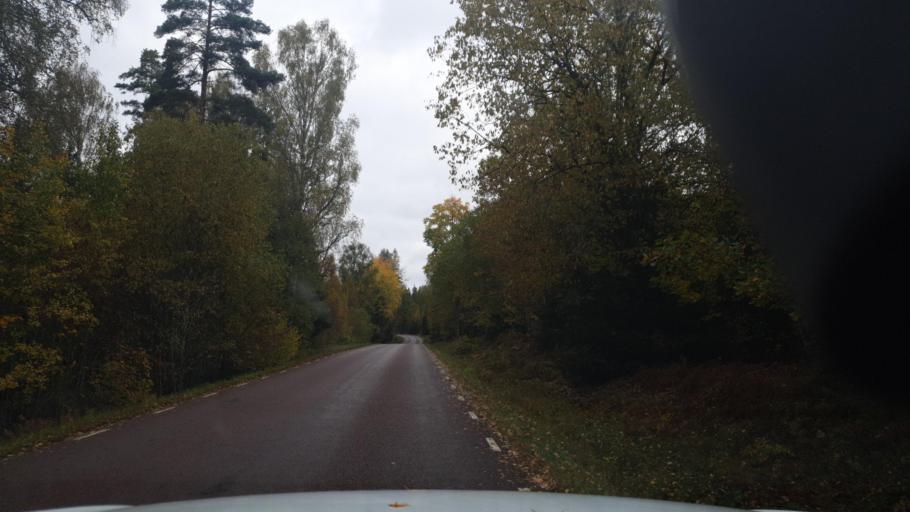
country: SE
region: Vaermland
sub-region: Grums Kommun
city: Grums
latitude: 59.4174
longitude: 13.0841
